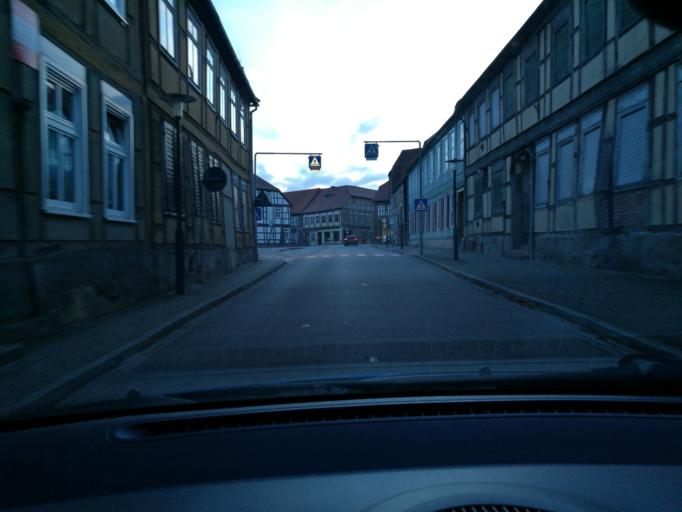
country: DE
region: Brandenburg
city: Lenzen
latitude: 53.0914
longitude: 11.4757
